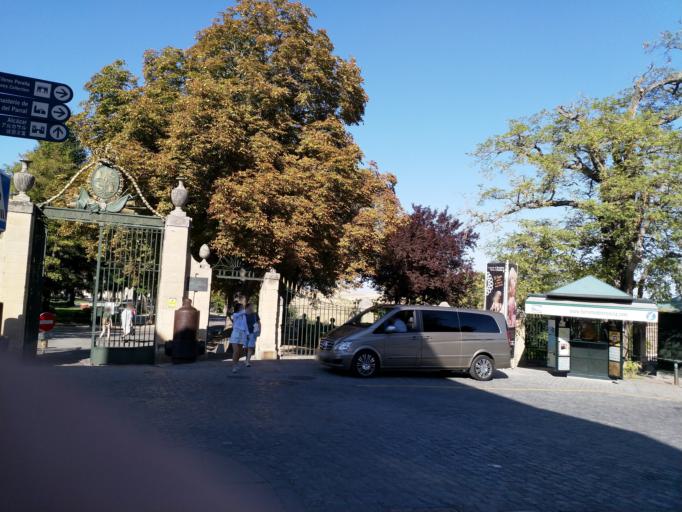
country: ES
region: Castille and Leon
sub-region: Provincia de Segovia
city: Segovia
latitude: 40.9524
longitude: -4.1300
